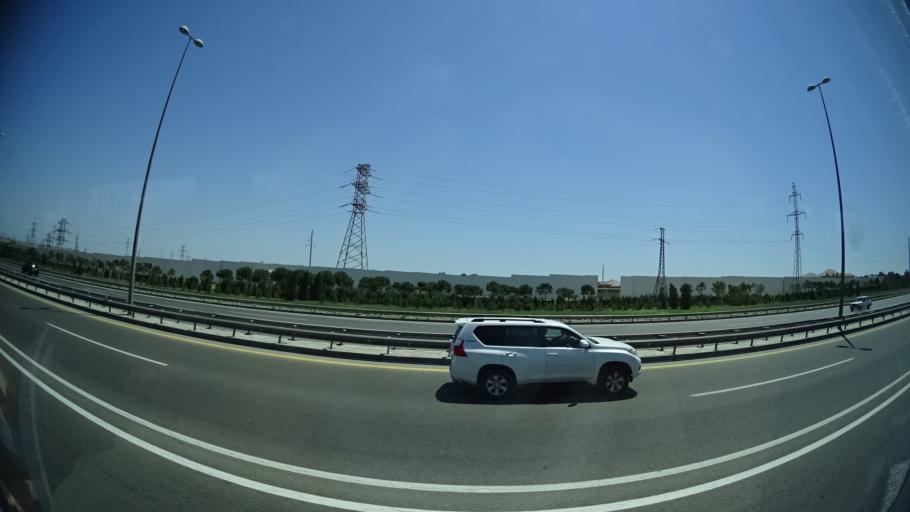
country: AZ
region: Baki
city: Yeni Suraxani
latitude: 40.4376
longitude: 50.0339
